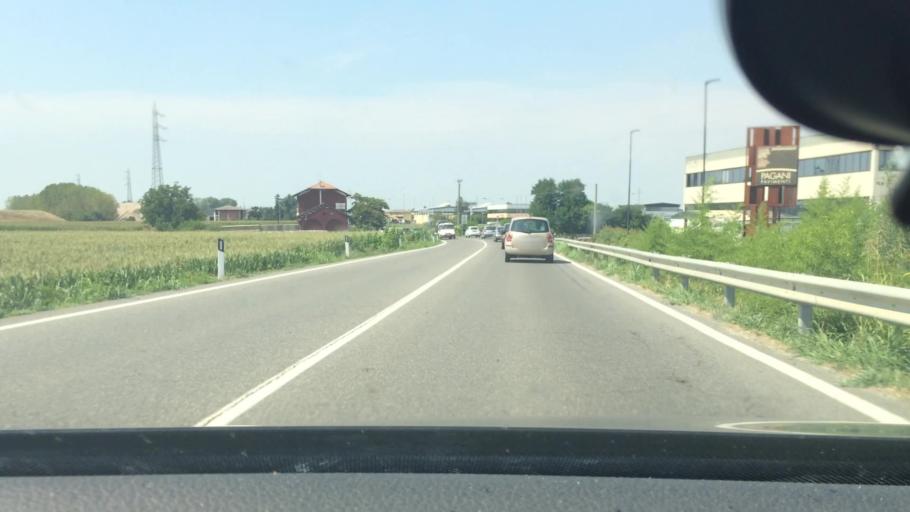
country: IT
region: Lombardy
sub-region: Provincia di Lodi
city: Guardamiglio
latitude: 45.0953
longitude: 9.6889
